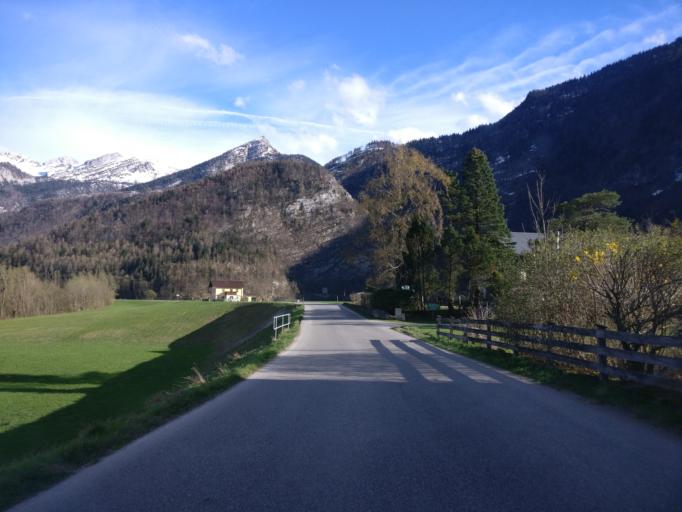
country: AT
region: Salzburg
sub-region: Politischer Bezirk Hallein
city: Golling an der Salzach
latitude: 47.5851
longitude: 13.1591
